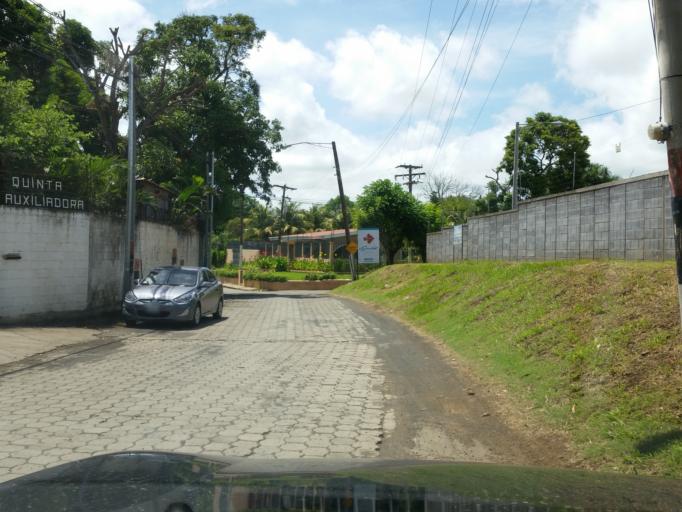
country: NI
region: Managua
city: Managua
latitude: 12.0815
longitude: -86.2367
